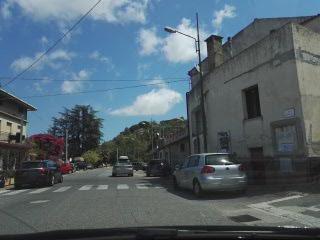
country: IT
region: Calabria
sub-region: Provincia di Vibo-Valentia
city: Ricadi
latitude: 38.6060
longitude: 15.8715
